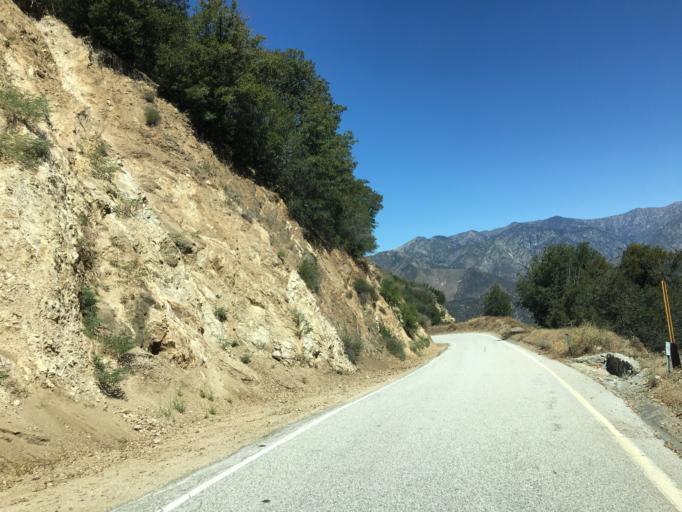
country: US
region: California
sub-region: San Bernardino County
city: San Antonio Heights
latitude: 34.2219
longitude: -117.7224
